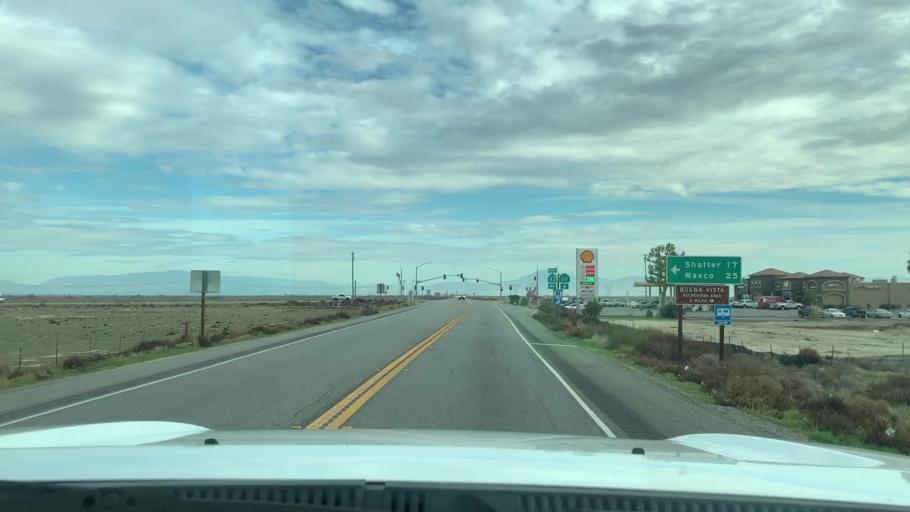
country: US
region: California
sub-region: Kern County
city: Rosedale
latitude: 35.2674
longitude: -119.2551
